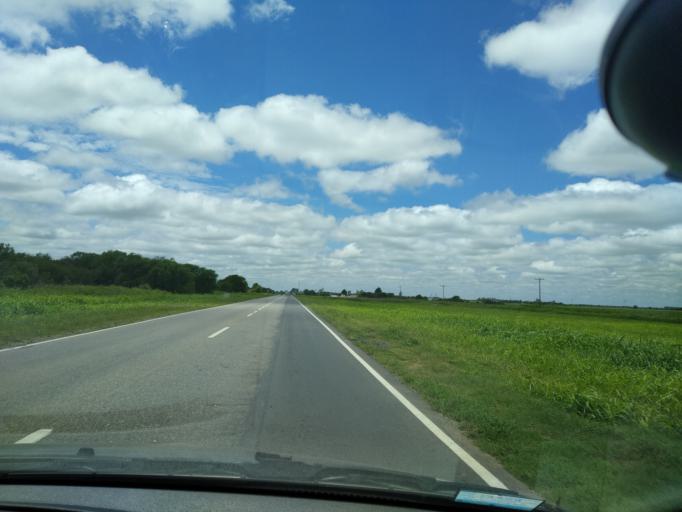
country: AR
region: Cordoba
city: Toledo
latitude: -31.6486
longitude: -64.1124
